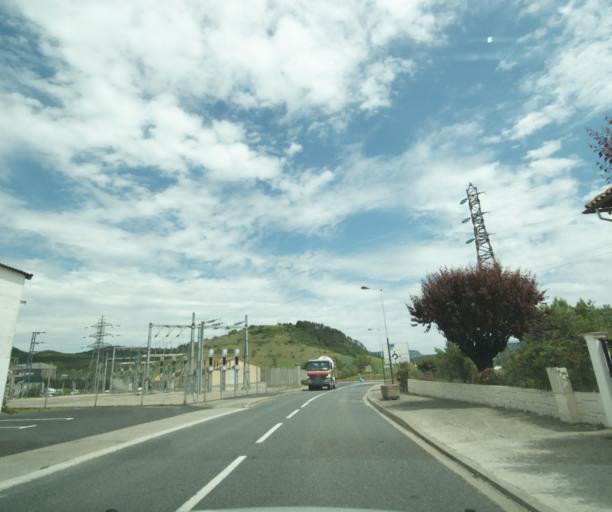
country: FR
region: Midi-Pyrenees
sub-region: Departement de l'Aveyron
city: Saint-Affrique
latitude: 43.9747
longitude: 2.9614
